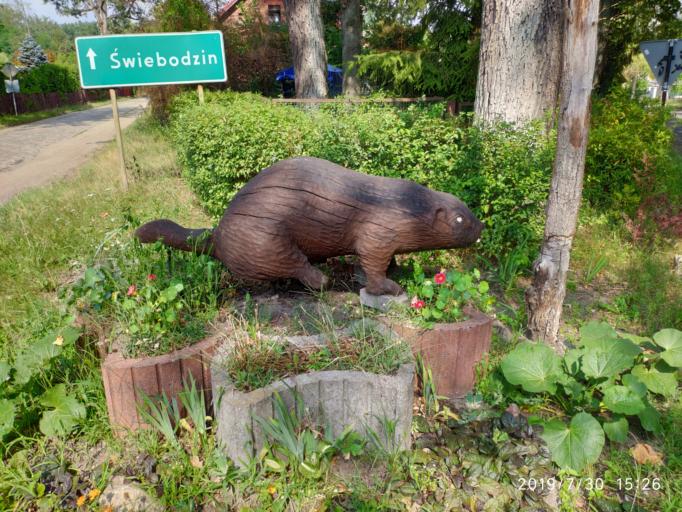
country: PL
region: Lubusz
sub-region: Powiat krosnienski
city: Bytnica
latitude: 52.1847
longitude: 15.2750
